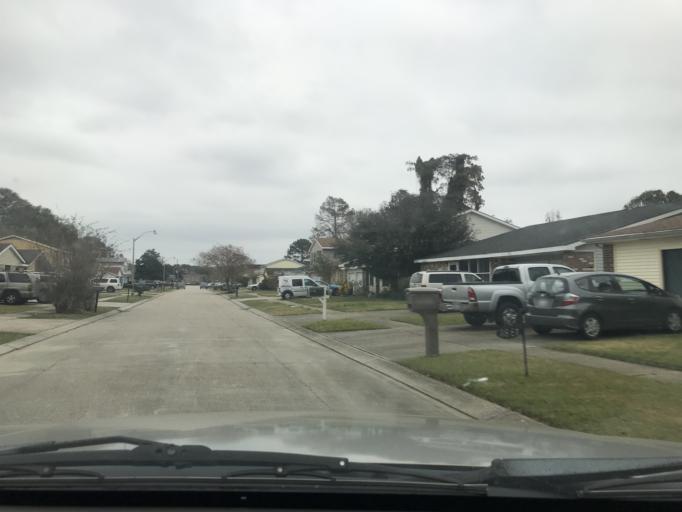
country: US
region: Louisiana
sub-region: Jefferson Parish
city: Woodmere
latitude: 29.8610
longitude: -90.0780
